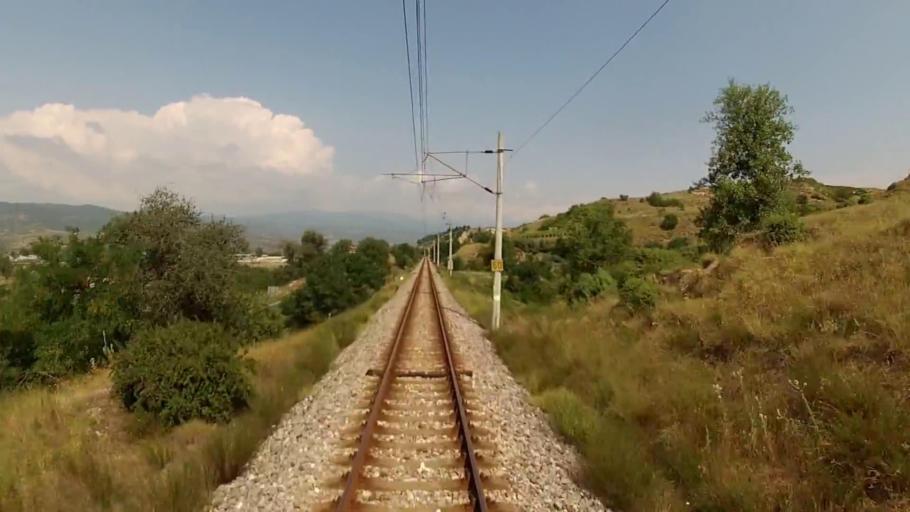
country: BG
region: Blagoevgrad
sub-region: Obshtina Strumyani
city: Strumyani
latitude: 41.6227
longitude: 23.2163
